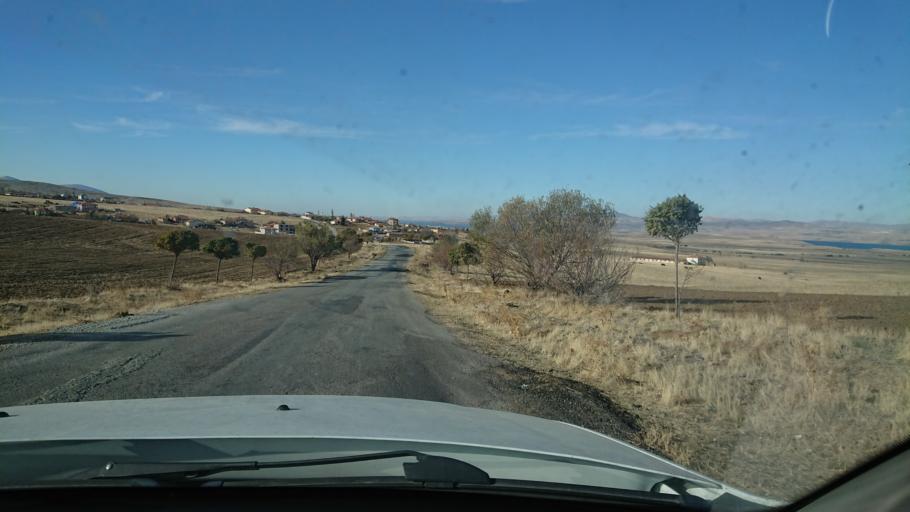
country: TR
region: Aksaray
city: Sariyahsi
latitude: 38.9742
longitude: 33.8587
